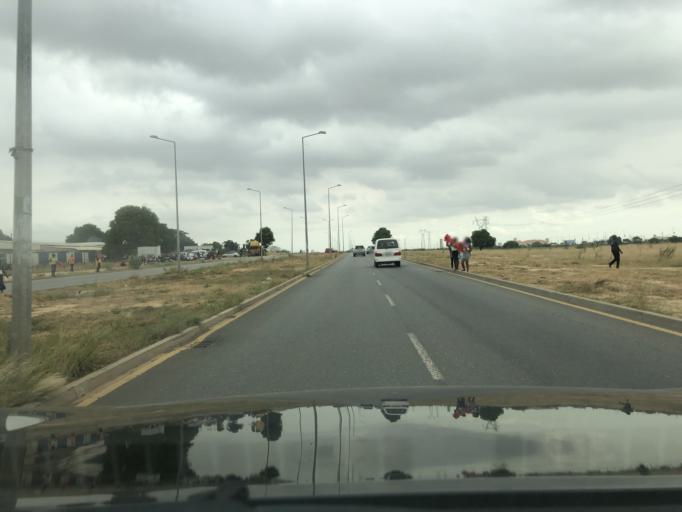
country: AO
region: Luanda
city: Luanda
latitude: -8.9757
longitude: 13.2826
